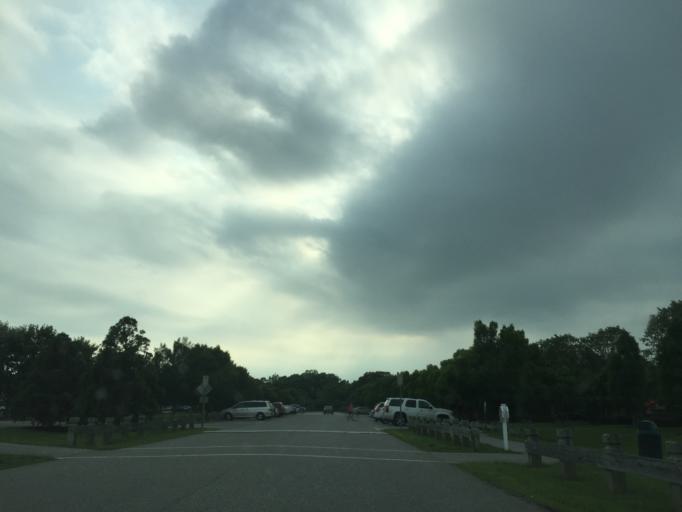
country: US
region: Virginia
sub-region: Isle of Wight County
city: Carrollton
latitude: 37.0910
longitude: -76.5286
